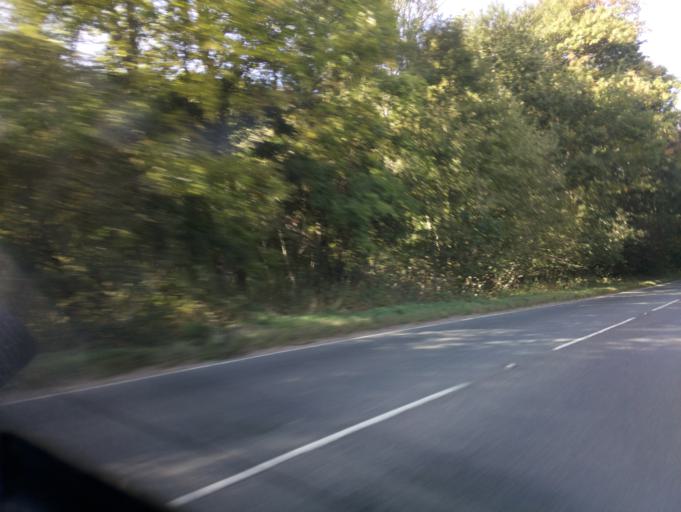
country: GB
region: England
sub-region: Hampshire
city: Tadley
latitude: 51.3110
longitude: -1.1161
